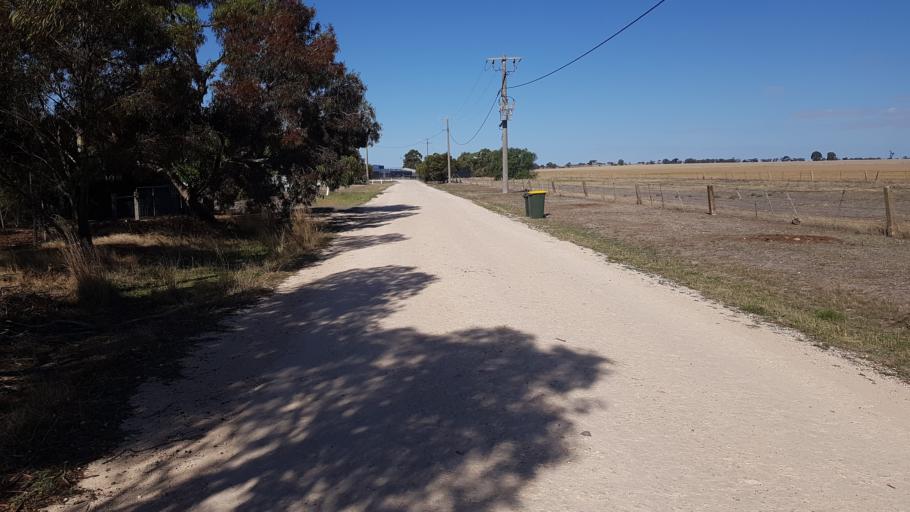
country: AU
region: Victoria
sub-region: Horsham
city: Horsham
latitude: -36.7434
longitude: 141.9450
